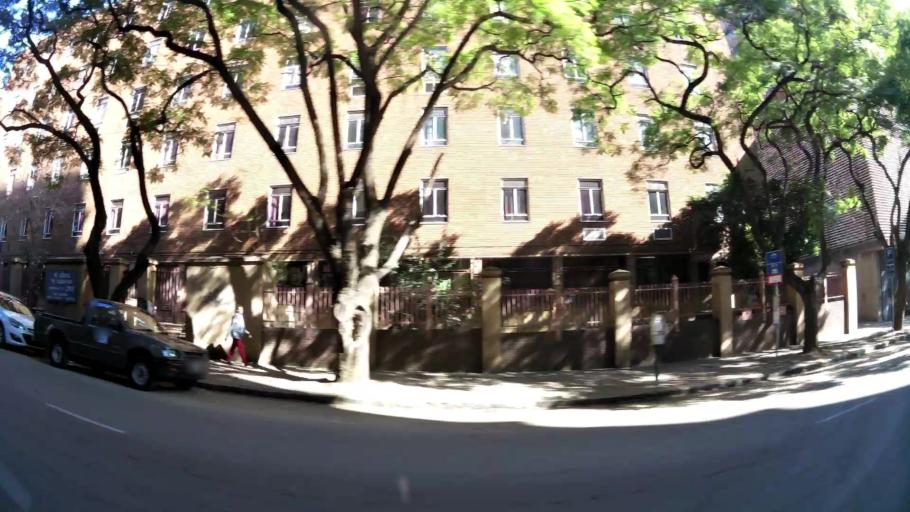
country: ZA
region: Gauteng
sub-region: City of Tshwane Metropolitan Municipality
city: Pretoria
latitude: -25.7490
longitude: 28.1858
